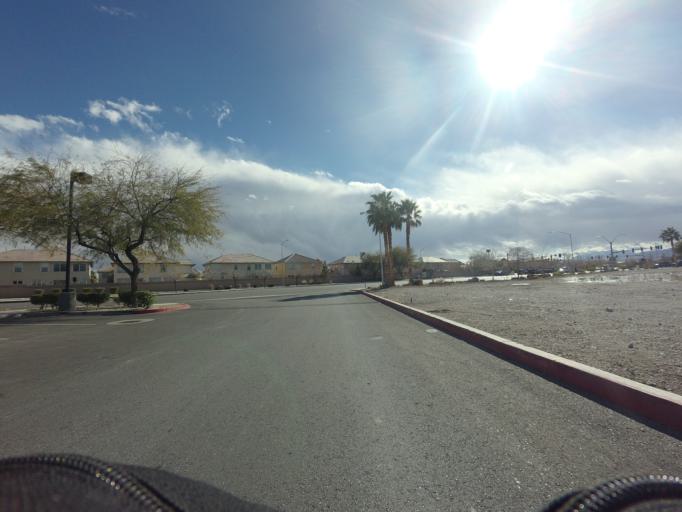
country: US
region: Nevada
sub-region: Clark County
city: Nellis Air Force Base
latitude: 36.2638
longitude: -115.1159
